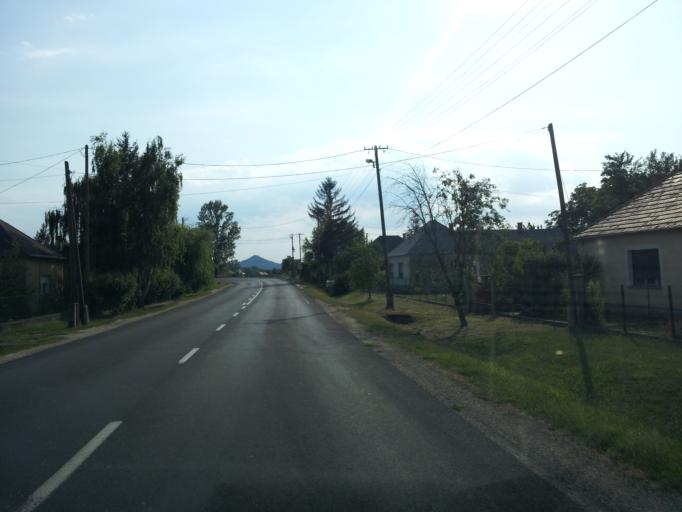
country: HU
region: Veszprem
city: Revfueloep
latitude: 46.9292
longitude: 17.5609
